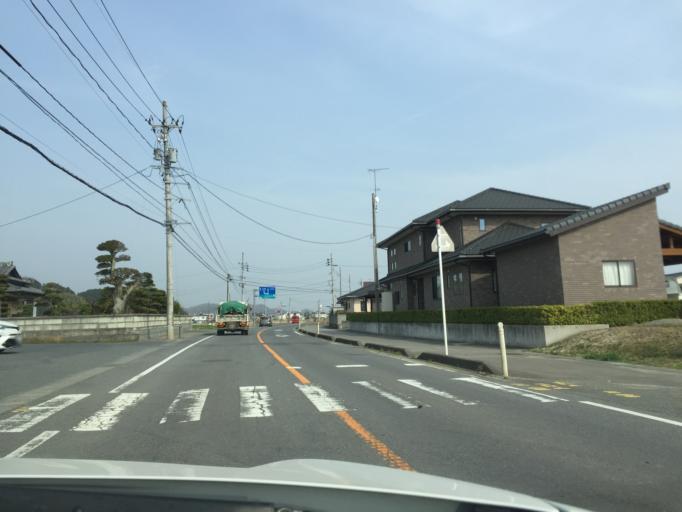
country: JP
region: Fukushima
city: Iwaki
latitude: 36.9596
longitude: 140.8386
